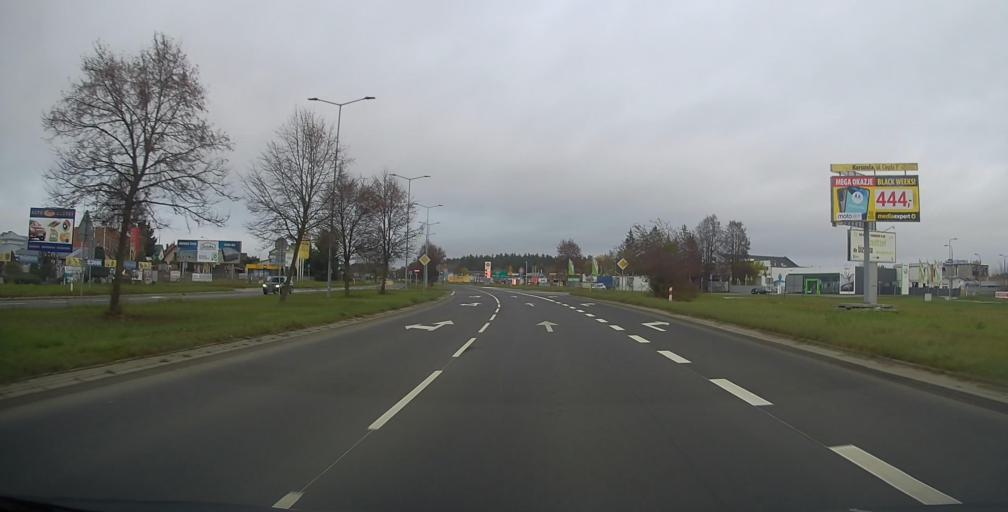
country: PL
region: Warmian-Masurian Voivodeship
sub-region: Powiat elcki
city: Elk
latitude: 53.8301
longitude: 22.3923
